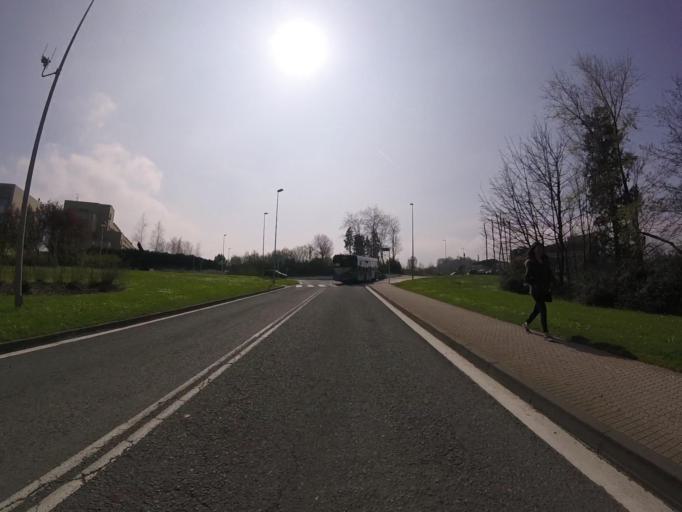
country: ES
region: Basque Country
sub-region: Provincia de Guipuzcoa
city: Hernani
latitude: 43.2883
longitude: -1.9829
